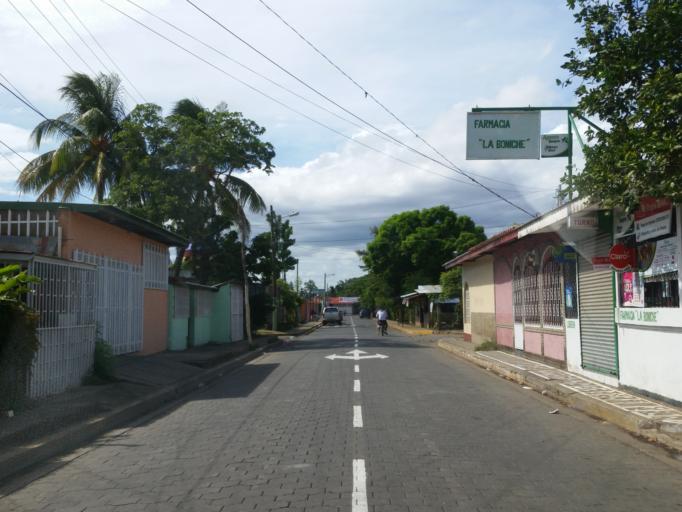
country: NI
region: Masaya
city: Nindiri
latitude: 12.0020
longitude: -86.1158
